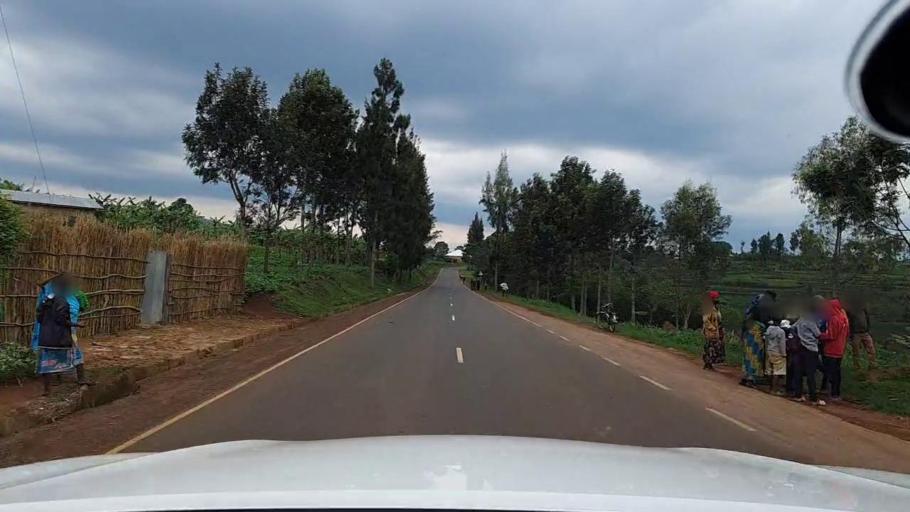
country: RW
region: Western Province
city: Cyangugu
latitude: -2.5942
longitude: 28.9274
